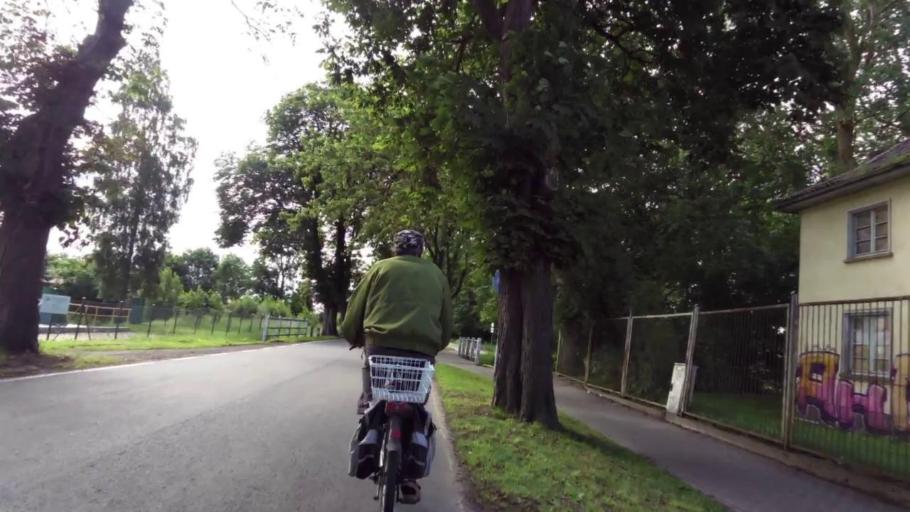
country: PL
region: West Pomeranian Voivodeship
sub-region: Powiat slawienski
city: Darlowo
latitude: 54.4357
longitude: 16.3901
